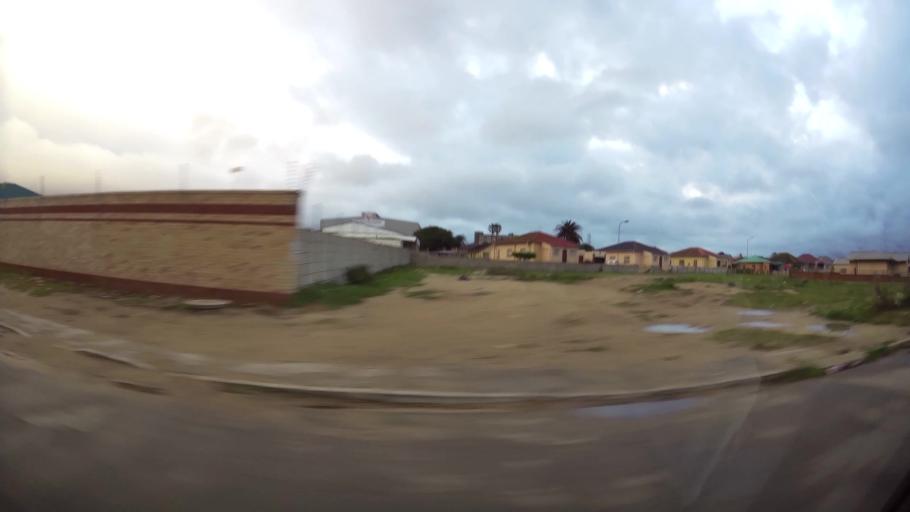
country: ZA
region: Eastern Cape
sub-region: Nelson Mandela Bay Metropolitan Municipality
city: Port Elizabeth
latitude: -33.9269
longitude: 25.6047
